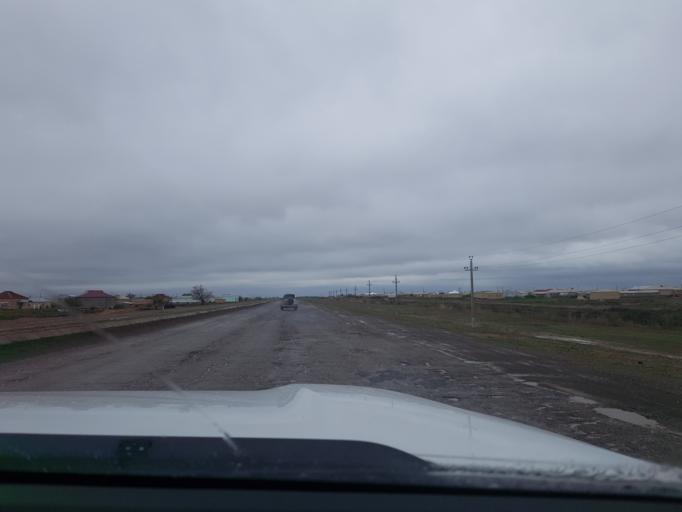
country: TM
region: Mary
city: Bayramaly
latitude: 37.6064
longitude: 62.1180
